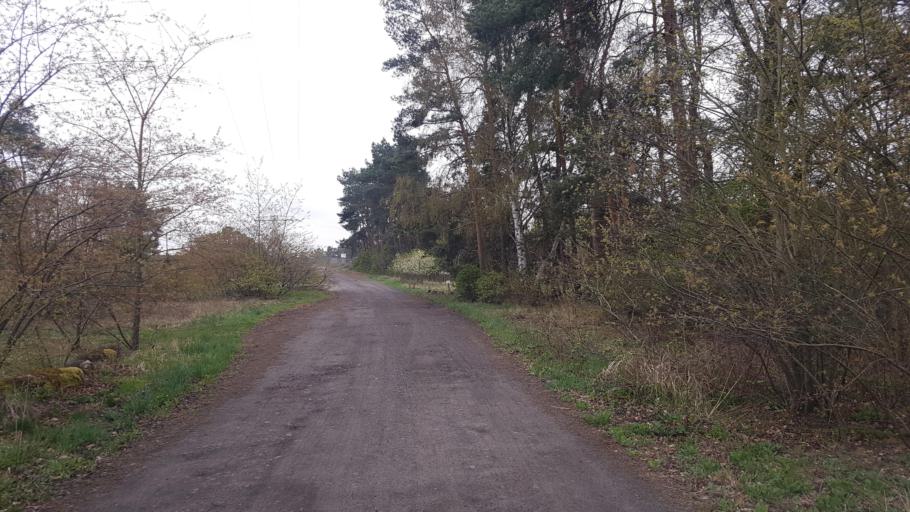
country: DE
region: Brandenburg
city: Luckenwalde
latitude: 52.0927
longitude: 13.1451
